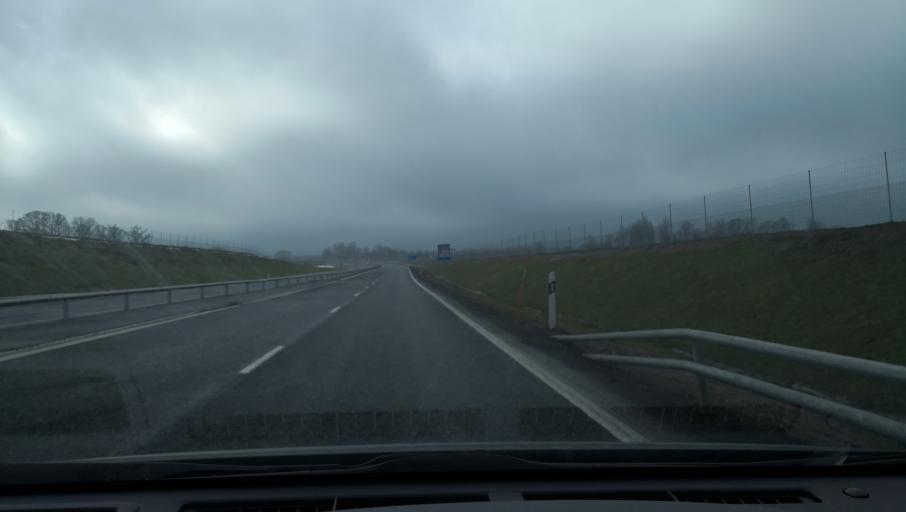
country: SE
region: Vaestra Goetaland
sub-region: Gullspangs Kommun
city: Hova
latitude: 58.8661
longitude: 14.2286
